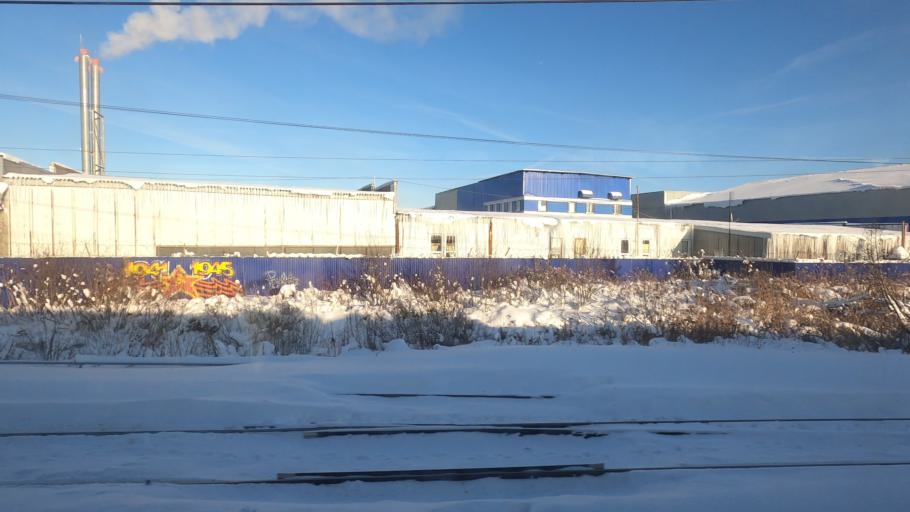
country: RU
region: Moskovskaya
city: Taldom
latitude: 56.7172
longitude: 37.5359
